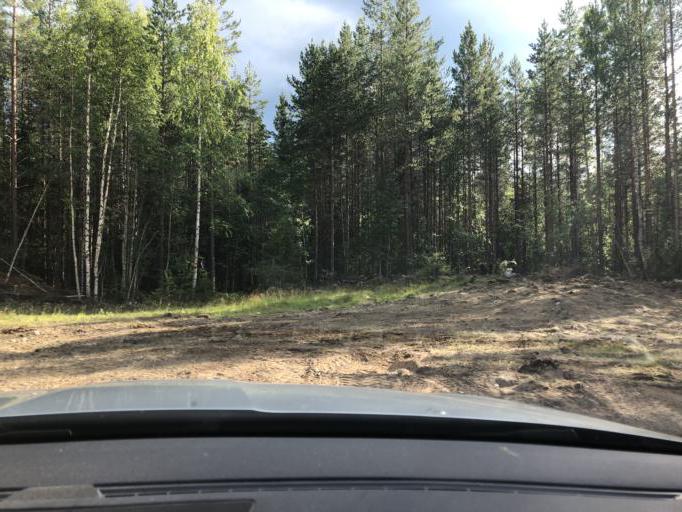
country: SE
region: Vaesternorrland
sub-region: Solleftea Kommun
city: Solleftea
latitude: 63.3107
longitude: 17.2834
